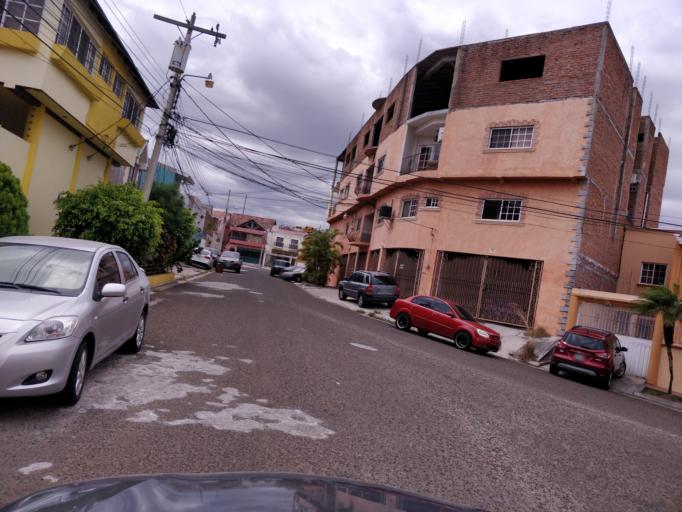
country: HN
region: Francisco Morazan
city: Yaguacire
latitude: 14.0470
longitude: -87.2175
